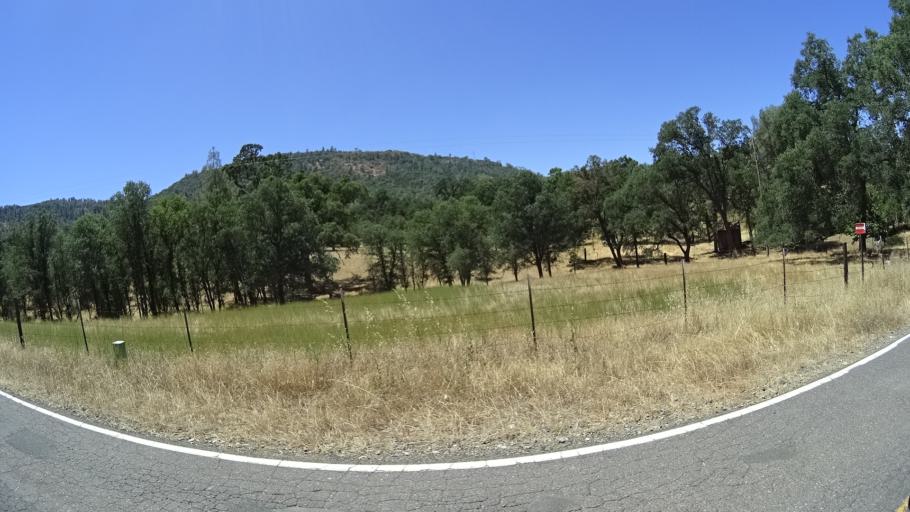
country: US
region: California
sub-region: Calaveras County
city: Copperopolis
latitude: 38.0760
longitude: -120.6653
